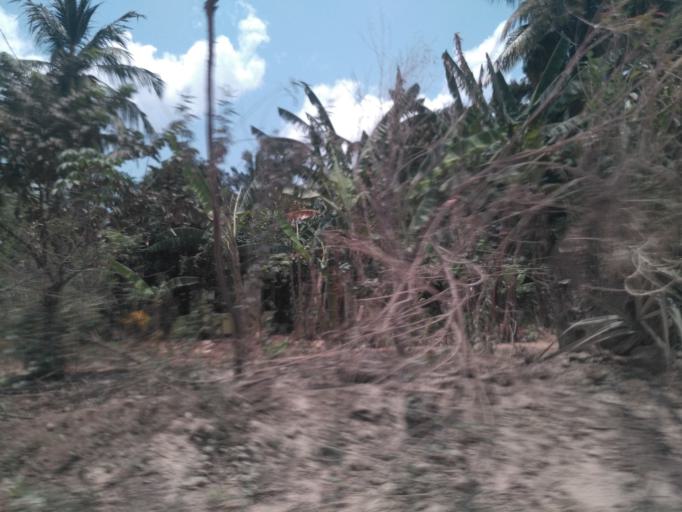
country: TZ
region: Dar es Salaam
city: Dar es Salaam
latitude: -6.8423
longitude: 39.3474
